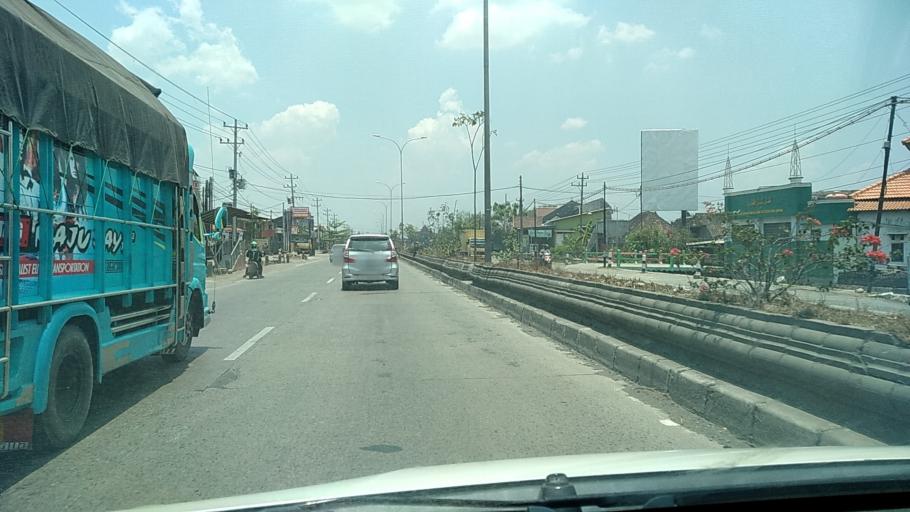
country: ID
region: Central Java
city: Semarang
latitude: -6.9542
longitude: 110.4735
